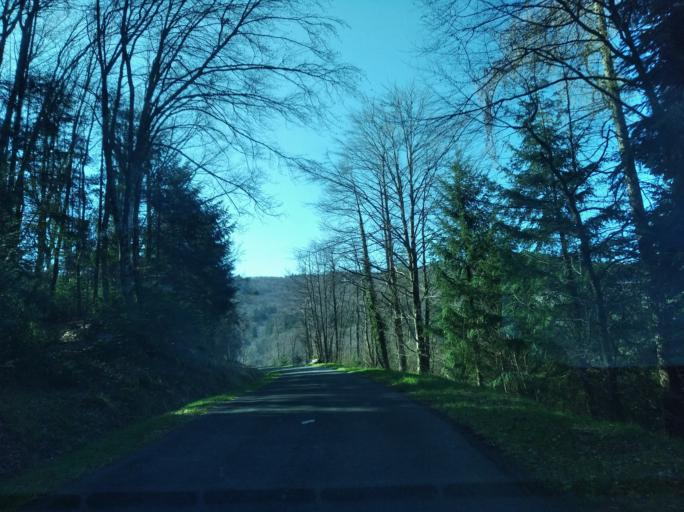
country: FR
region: Auvergne
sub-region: Departement de l'Allier
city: Le Mayet-de-Montagne
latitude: 46.1018
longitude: 3.7536
